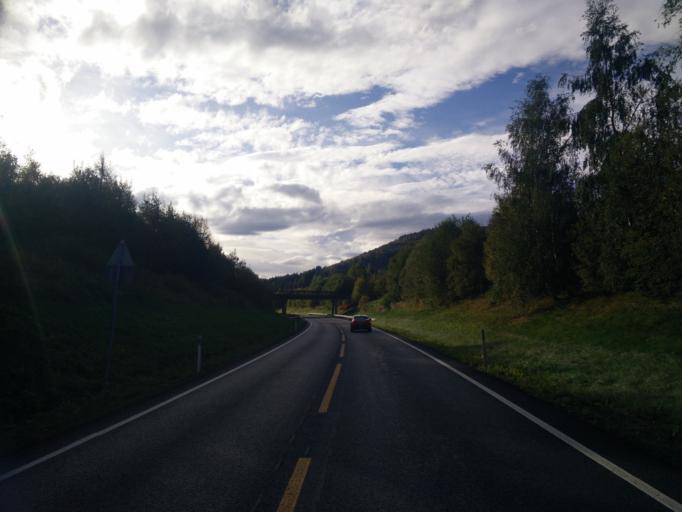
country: NO
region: More og Romsdal
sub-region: Vestnes
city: Vestnes
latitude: 62.6166
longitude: 7.0878
